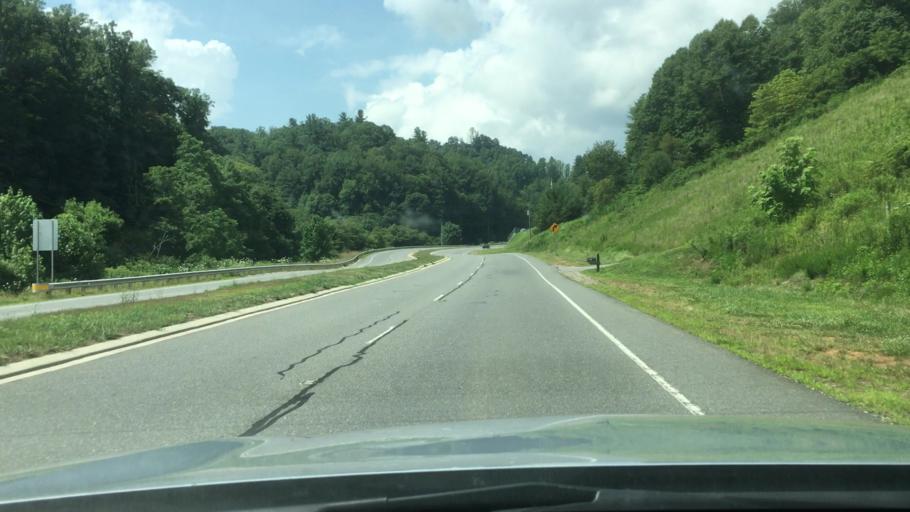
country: US
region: North Carolina
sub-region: Madison County
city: Mars Hill
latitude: 35.9129
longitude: -82.4658
